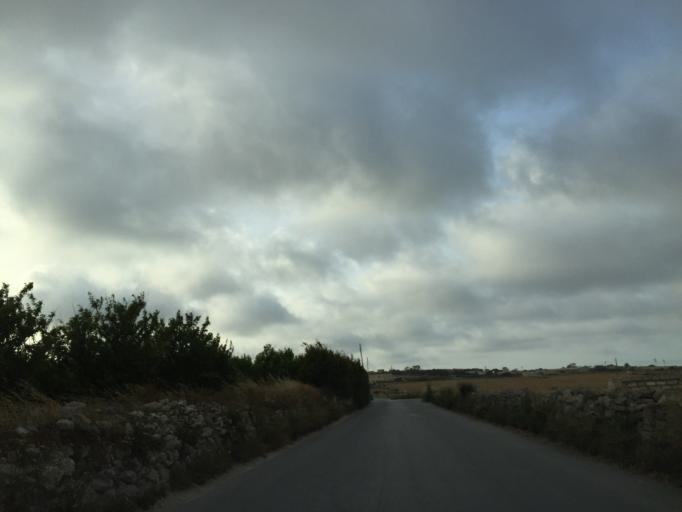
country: MT
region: L-Imdina
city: Imdina
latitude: 35.8756
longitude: 14.4132
